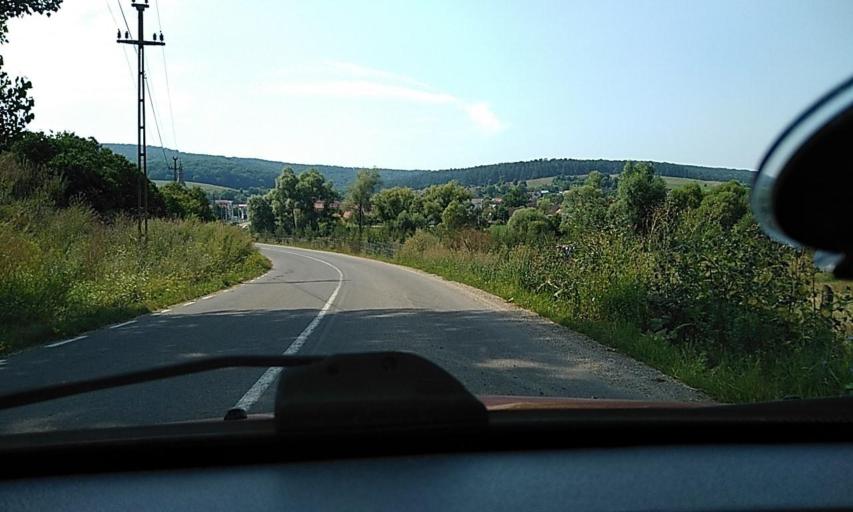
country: RO
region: Brasov
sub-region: Oras Rupea
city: Fiser
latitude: 46.0138
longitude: 25.1513
